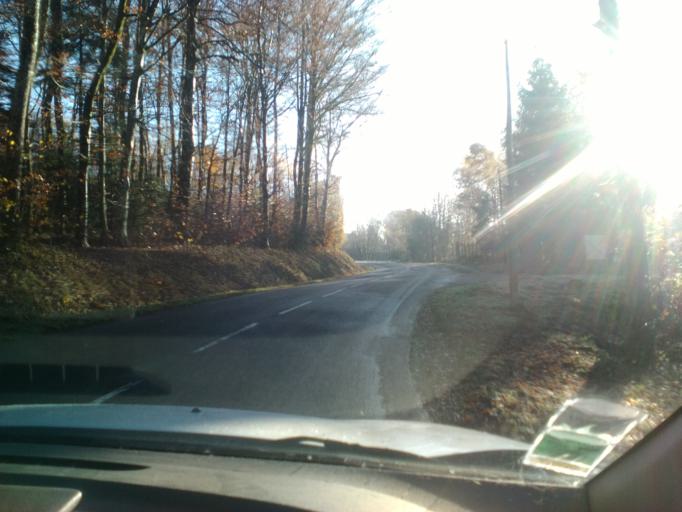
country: FR
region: Lorraine
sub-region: Departement des Vosges
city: Uzemain
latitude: 48.0562
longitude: 6.3663
